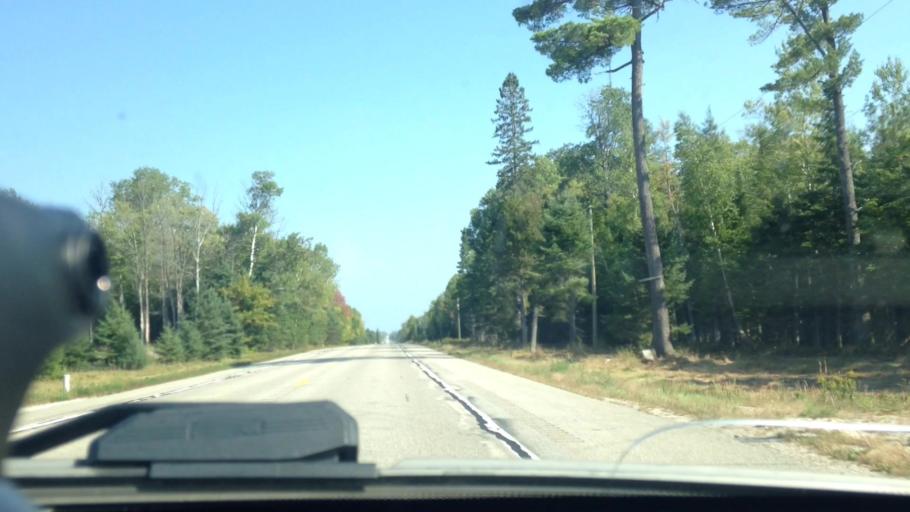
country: US
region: Michigan
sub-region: Luce County
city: Newberry
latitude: 46.3034
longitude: -85.3551
